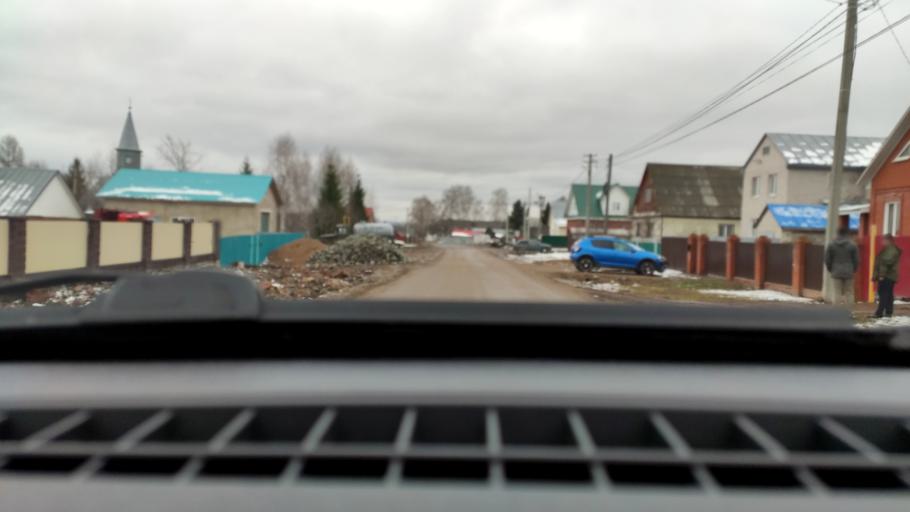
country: RU
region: Bashkortostan
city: Mikhaylovka
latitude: 54.8098
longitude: 55.8038
